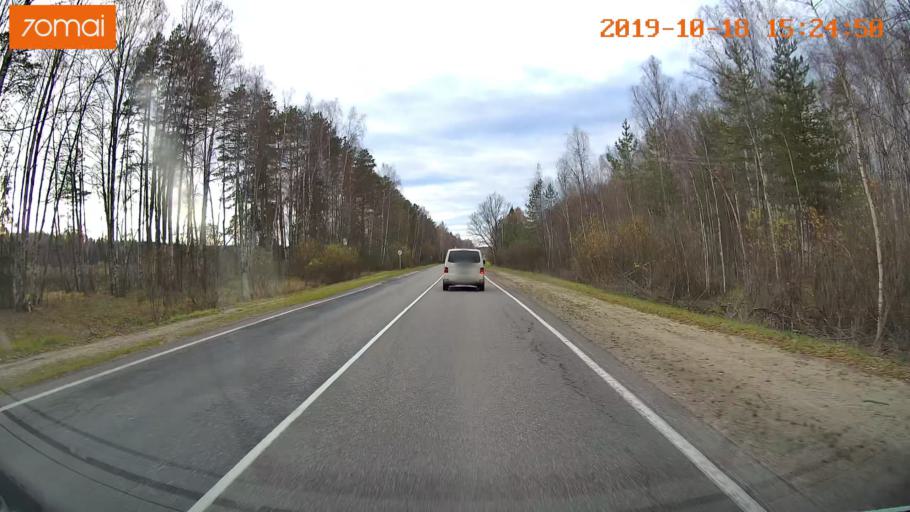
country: RU
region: Vladimir
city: Anopino
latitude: 55.7374
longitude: 40.7168
